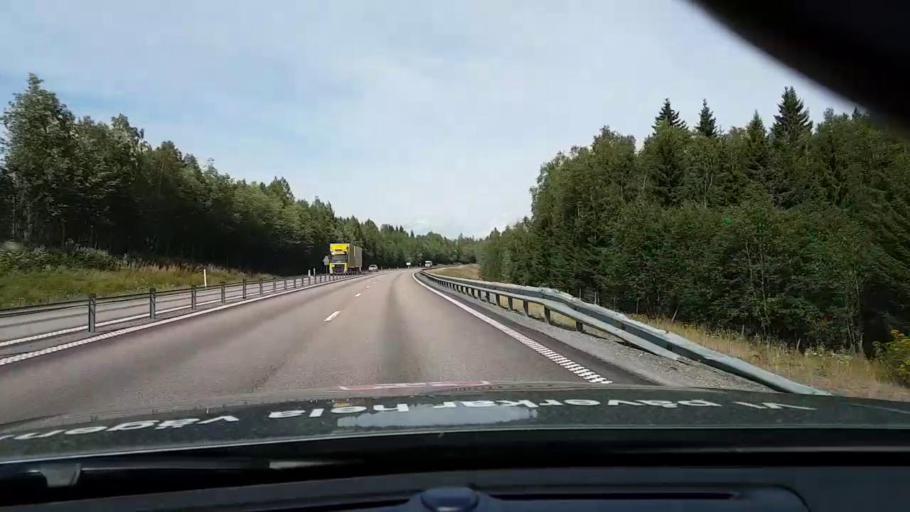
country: SE
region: Vaesternorrland
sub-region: OErnskoeldsviks Kommun
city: Husum
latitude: 63.4208
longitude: 19.2050
